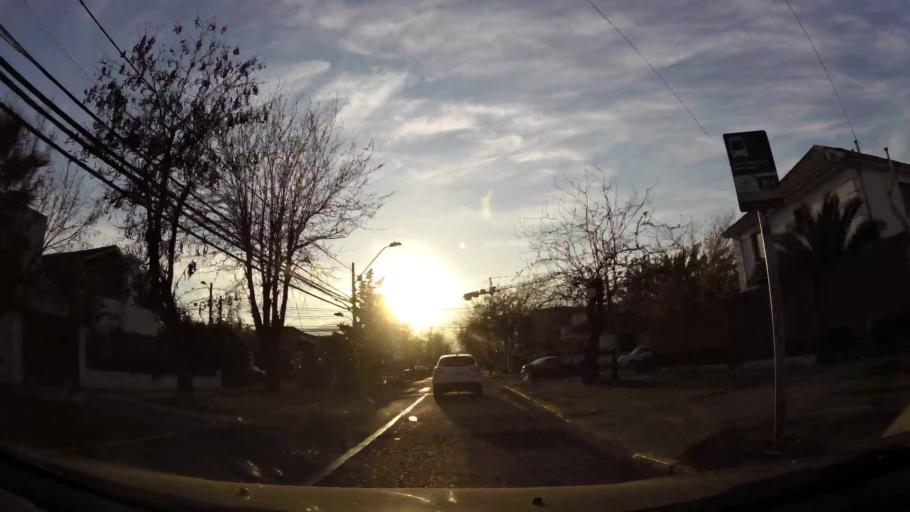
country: CL
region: Santiago Metropolitan
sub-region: Provincia de Santiago
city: Villa Presidente Frei, Nunoa, Santiago, Chile
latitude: -33.4485
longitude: -70.5886
